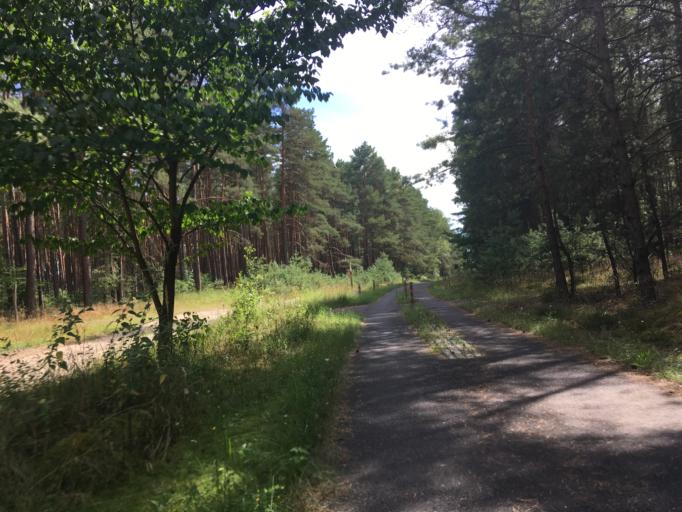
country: DE
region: Brandenburg
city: Rheinsberg
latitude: 53.0606
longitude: 12.9088
